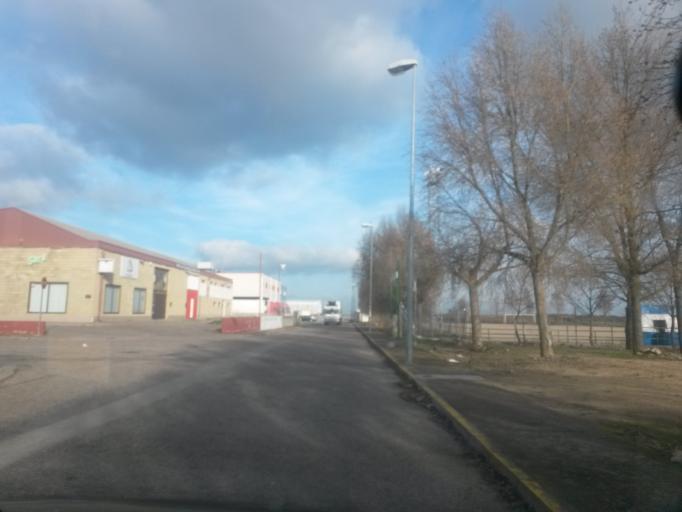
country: ES
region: Castille and Leon
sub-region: Provincia de Salamanca
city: San Cristobal de la Cuesta
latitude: 41.0067
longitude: -5.6111
